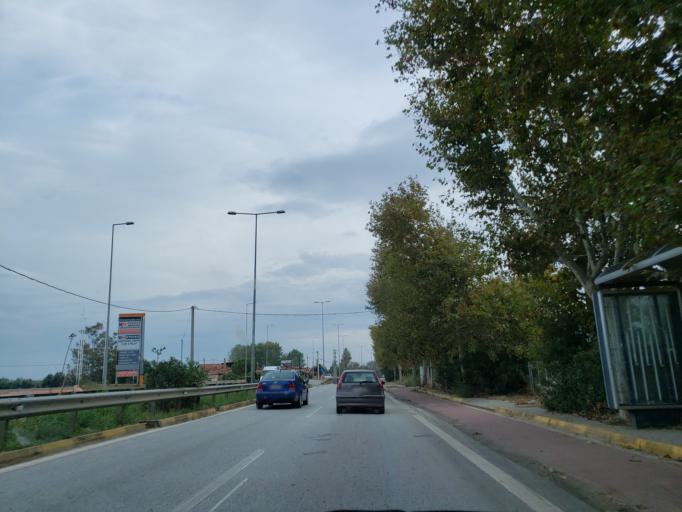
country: GR
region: Attica
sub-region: Nomarchia Anatolikis Attikis
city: Aghios Panteleimon
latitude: 38.1238
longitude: 23.9694
